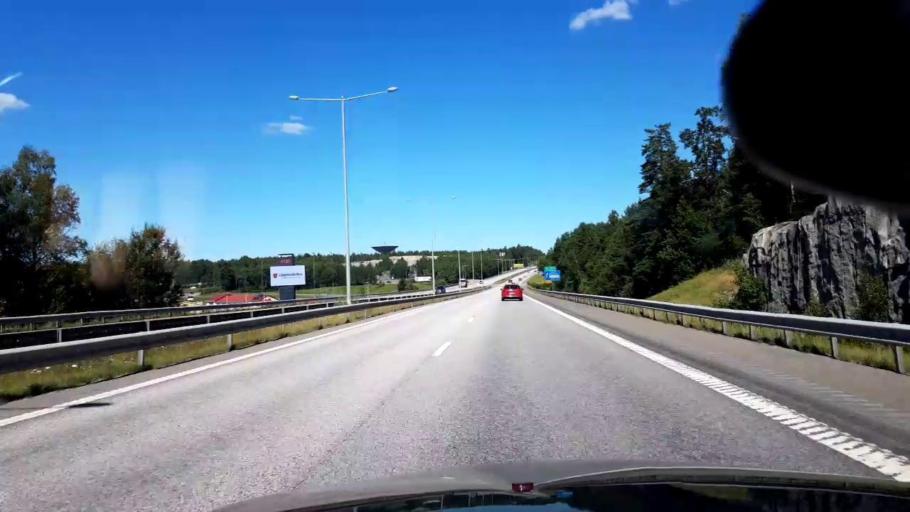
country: SE
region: Stockholm
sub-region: Upplands-Bro Kommun
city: Kungsaengen
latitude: 59.4900
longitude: 17.7523
